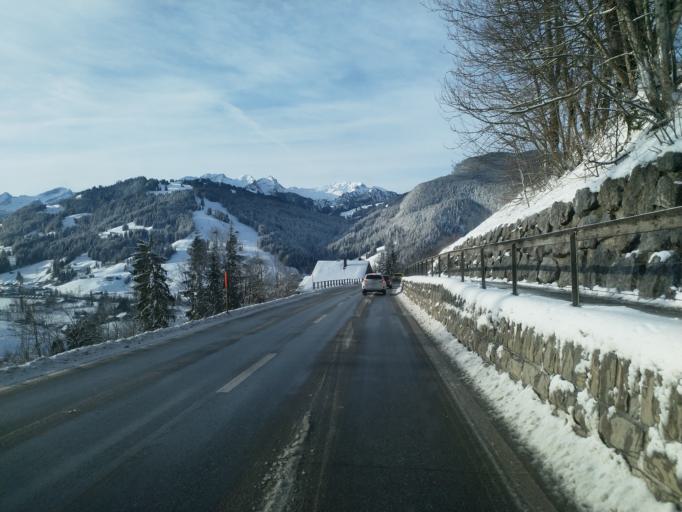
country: CH
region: Bern
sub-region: Obersimmental-Saanen District
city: Saanen
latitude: 46.4946
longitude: 7.2736
